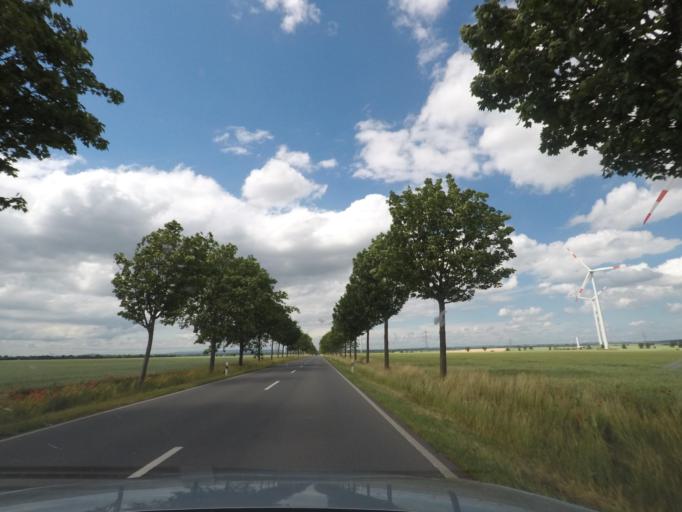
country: DE
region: Saxony-Anhalt
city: Schwanebeck
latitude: 51.9901
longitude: 11.1181
